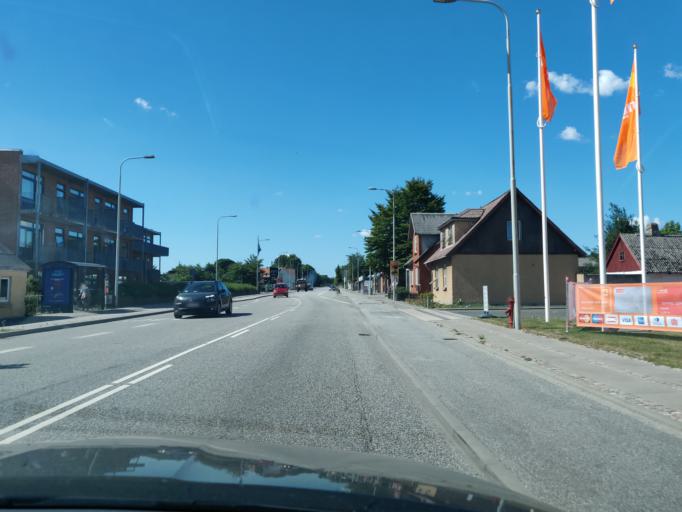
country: DK
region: North Denmark
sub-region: Alborg Kommune
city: Aalborg
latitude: 57.0685
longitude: 9.9452
